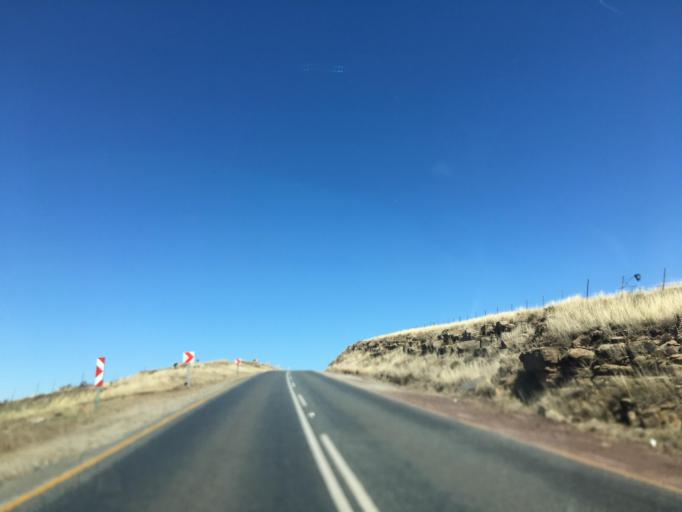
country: ZA
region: Eastern Cape
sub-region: Chris Hani District Municipality
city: Cofimvaba
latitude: -31.9090
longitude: 27.8380
